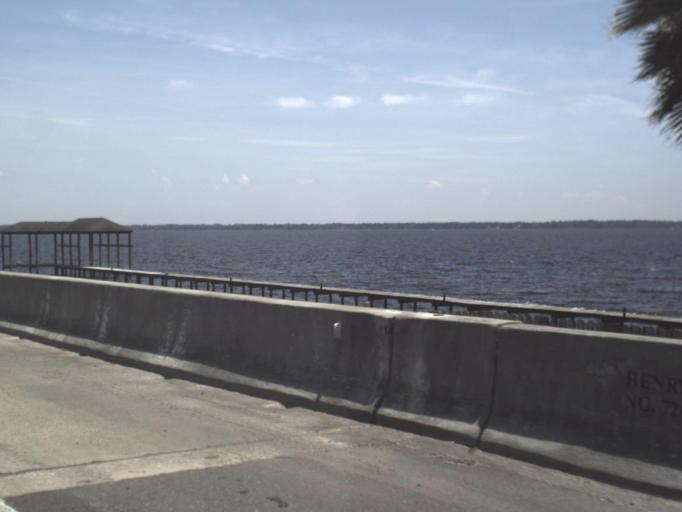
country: US
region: Florida
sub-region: Clay County
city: Orange Park
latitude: 30.1911
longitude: -81.6920
